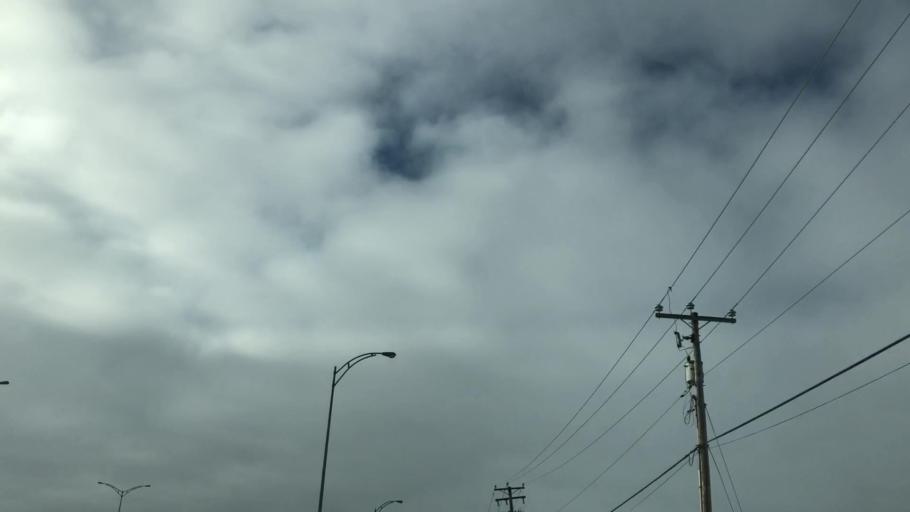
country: CA
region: Quebec
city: Sainte-Anne-de-Bellevue
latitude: 45.4222
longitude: -73.9642
